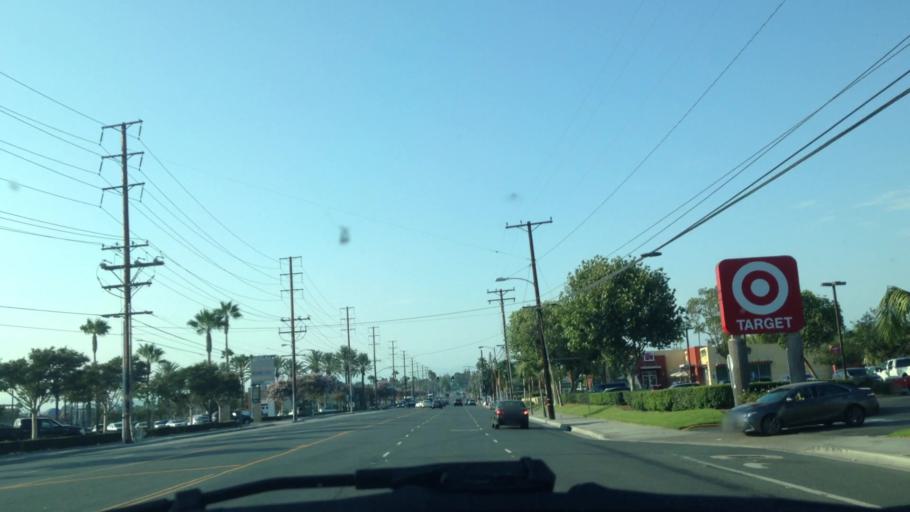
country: US
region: California
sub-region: Orange County
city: Villa Park
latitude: 33.8238
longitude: -117.8360
